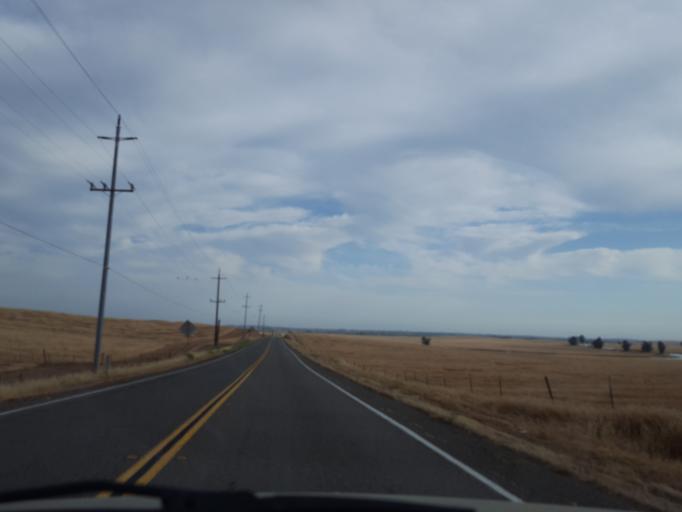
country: US
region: California
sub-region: Merced County
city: Merced
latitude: 37.4202
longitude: -120.4462
